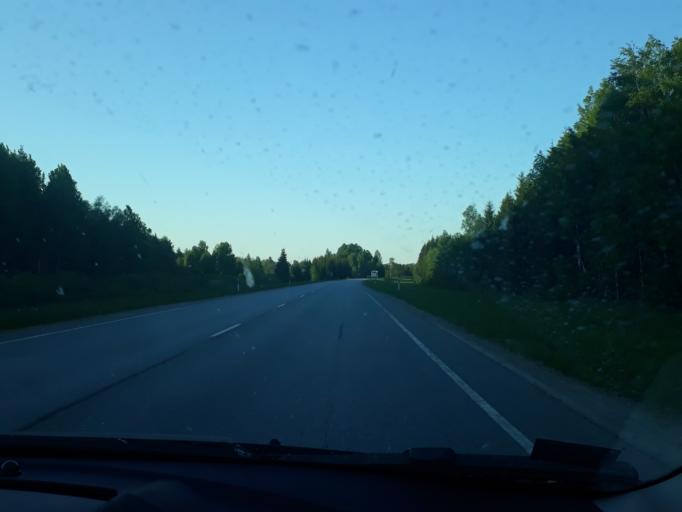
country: EE
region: Paernumaa
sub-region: Sindi linn
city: Sindi
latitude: 58.4596
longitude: 24.6990
